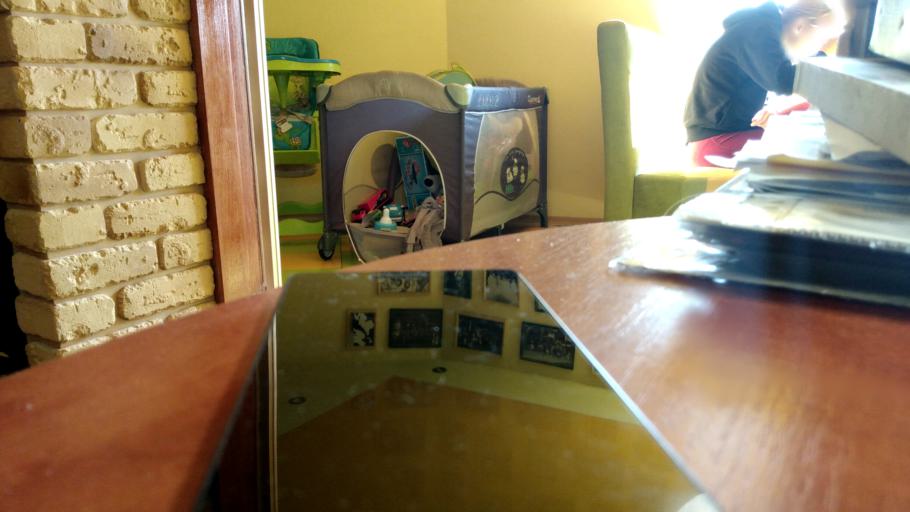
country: RU
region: Penza
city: Serdobsk
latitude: 52.4000
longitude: 44.3276
